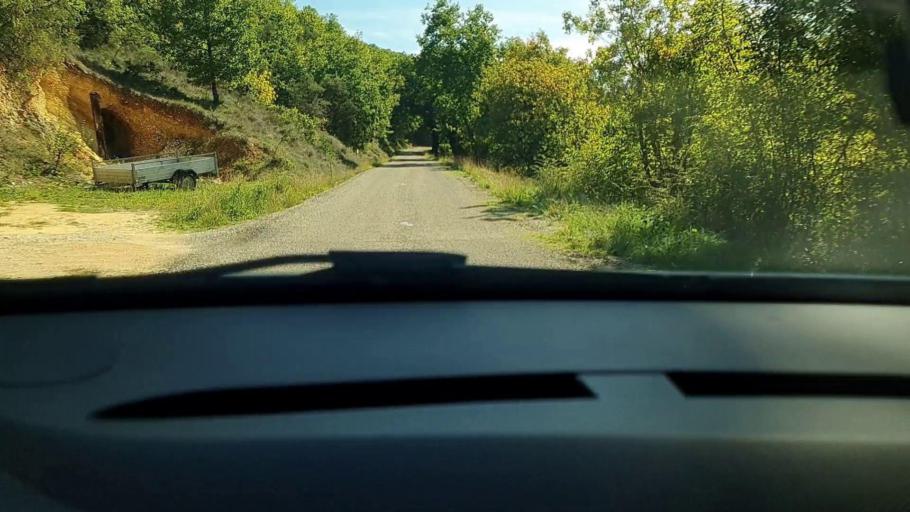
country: FR
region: Languedoc-Roussillon
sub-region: Departement du Gard
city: Saint-Ambroix
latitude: 44.2240
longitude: 4.2847
